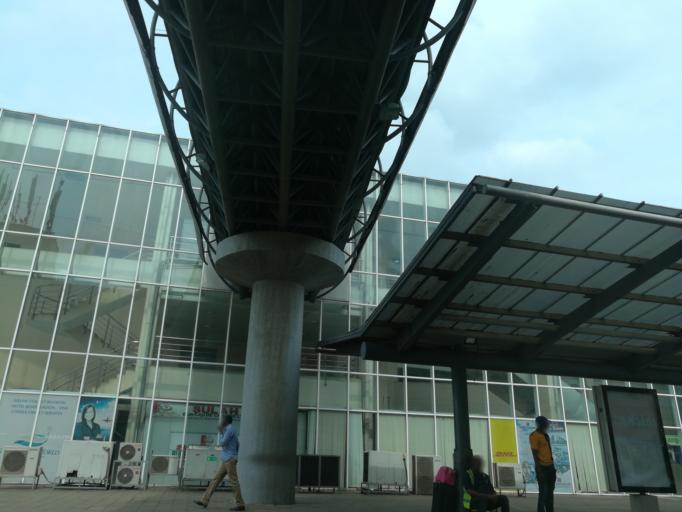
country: NG
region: Lagos
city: Ikeja
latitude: 6.5845
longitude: 3.3333
